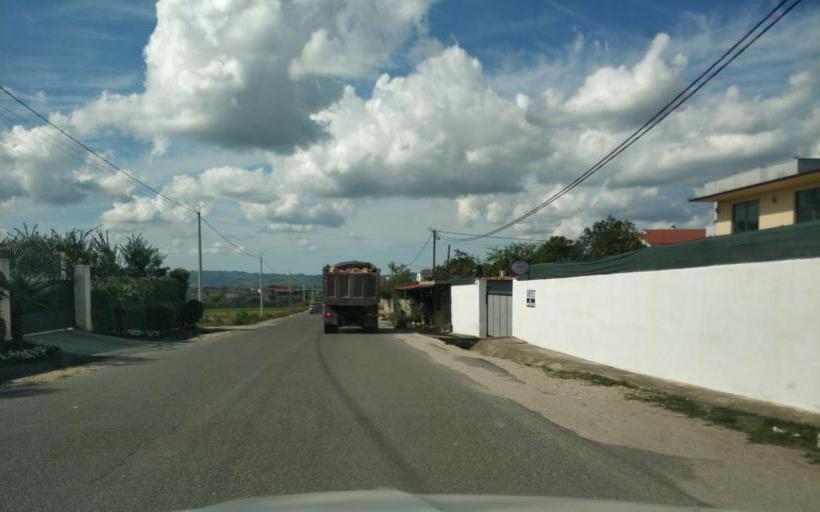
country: AL
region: Durres
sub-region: Rrethi i Krujes
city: Fushe-Kruje
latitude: 41.4780
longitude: 19.7387
